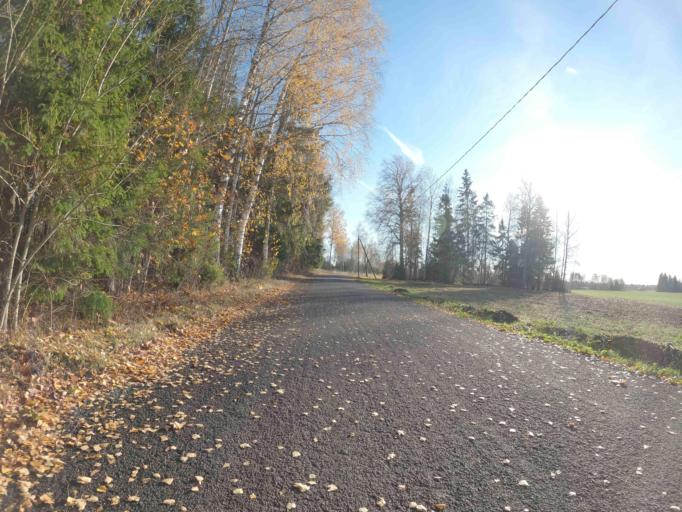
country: EE
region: Raplamaa
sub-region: Rapla vald
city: Rapla
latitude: 59.0189
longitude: 24.8018
